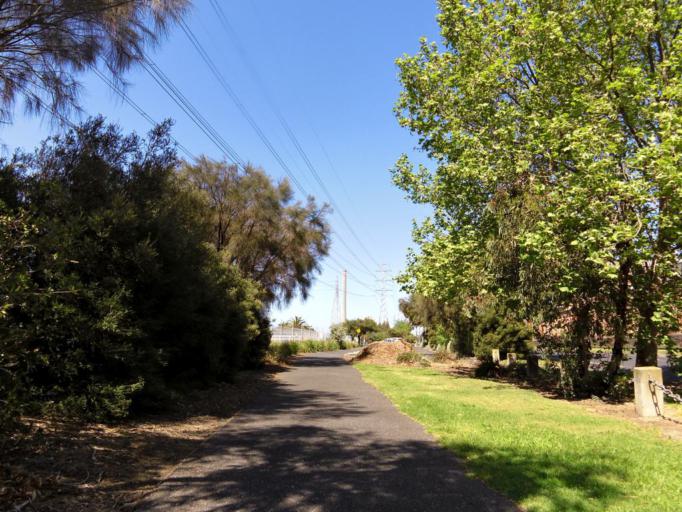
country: AU
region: Victoria
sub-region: Hobsons Bay
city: Spotswood
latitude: -37.8308
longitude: 144.8955
